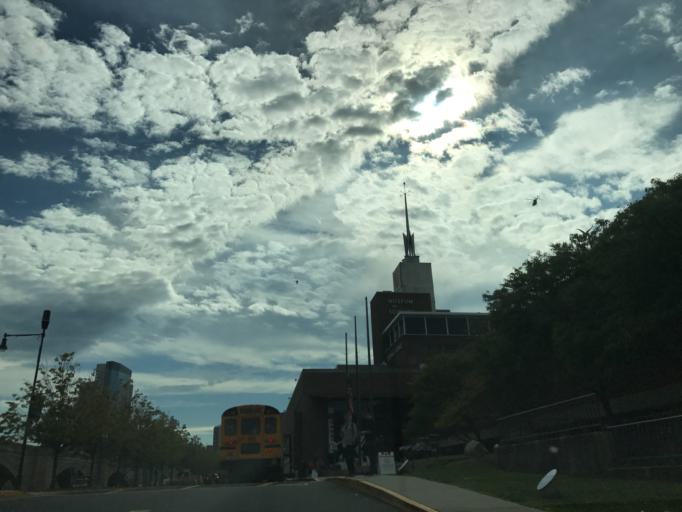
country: US
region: Massachusetts
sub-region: Suffolk County
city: Boston
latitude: 42.3682
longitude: -71.0717
